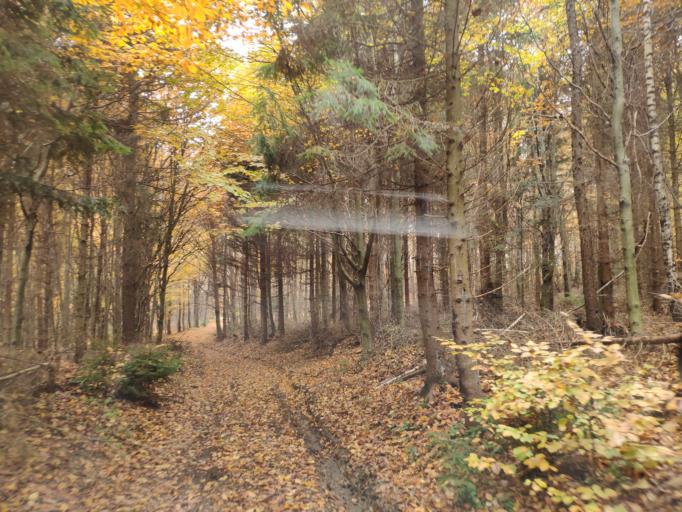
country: SK
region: Kosicky
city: Medzev
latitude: 48.7416
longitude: 20.9916
